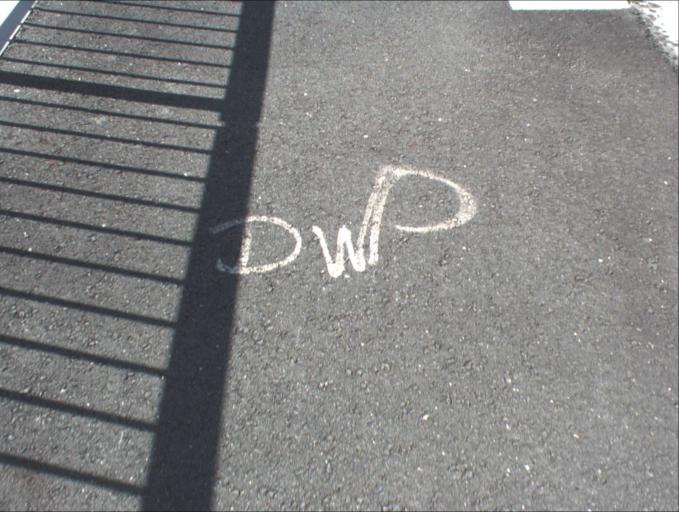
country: AU
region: Queensland
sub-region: Logan
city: Beenleigh
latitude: -27.6958
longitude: 153.1954
